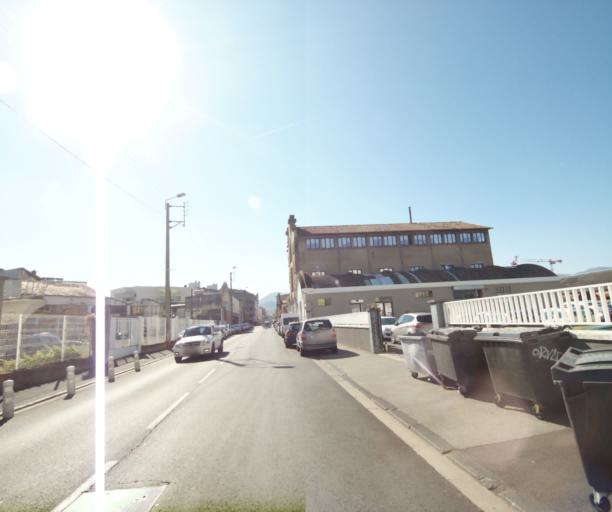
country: FR
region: Auvergne
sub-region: Departement du Puy-de-Dome
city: Clermont-Ferrand
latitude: 45.7816
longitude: 3.1108
